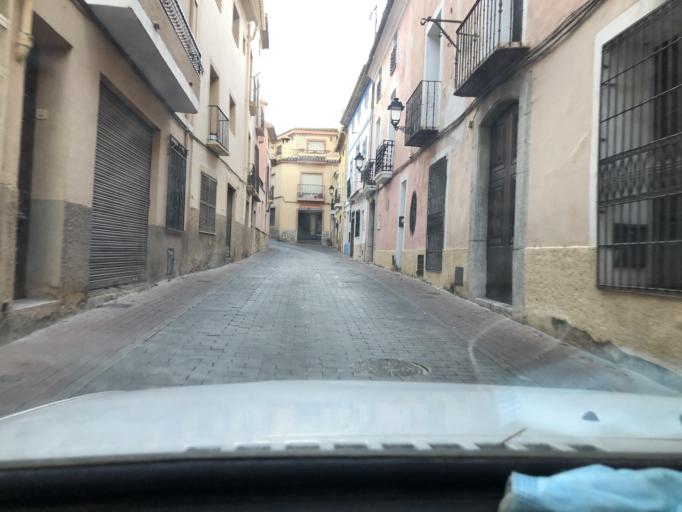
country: ES
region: Valencia
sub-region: Provincia de Alicante
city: Polop
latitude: 38.6220
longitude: -0.1278
